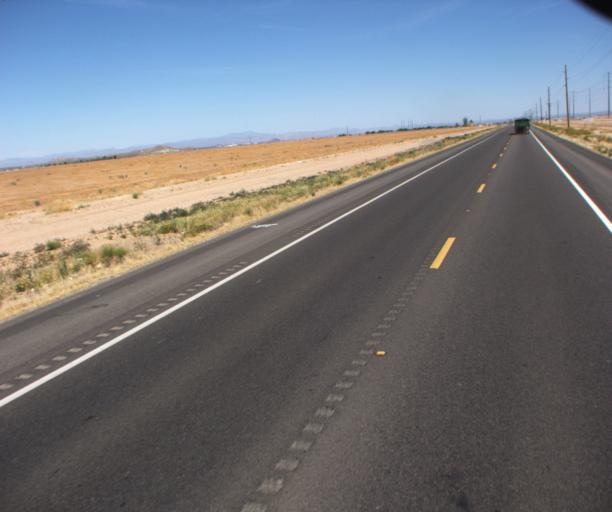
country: US
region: Arizona
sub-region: Pinal County
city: Blackwater
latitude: 33.0024
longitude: -111.5649
